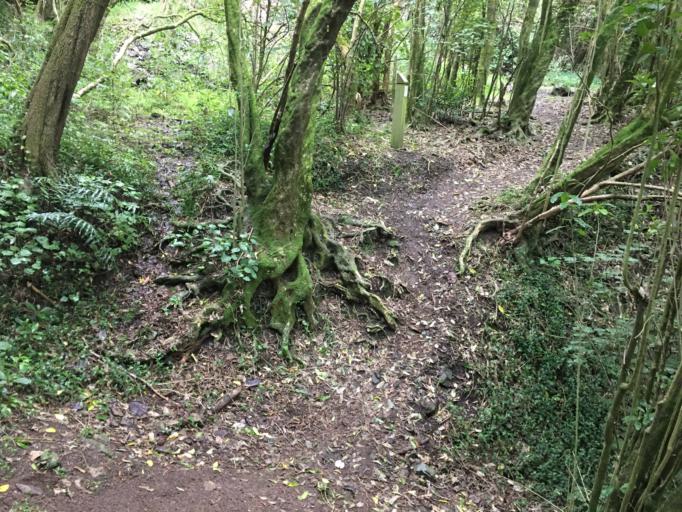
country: NZ
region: Wellington
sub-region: Wellington City
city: Kelburn
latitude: -41.2730
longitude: 174.7701
